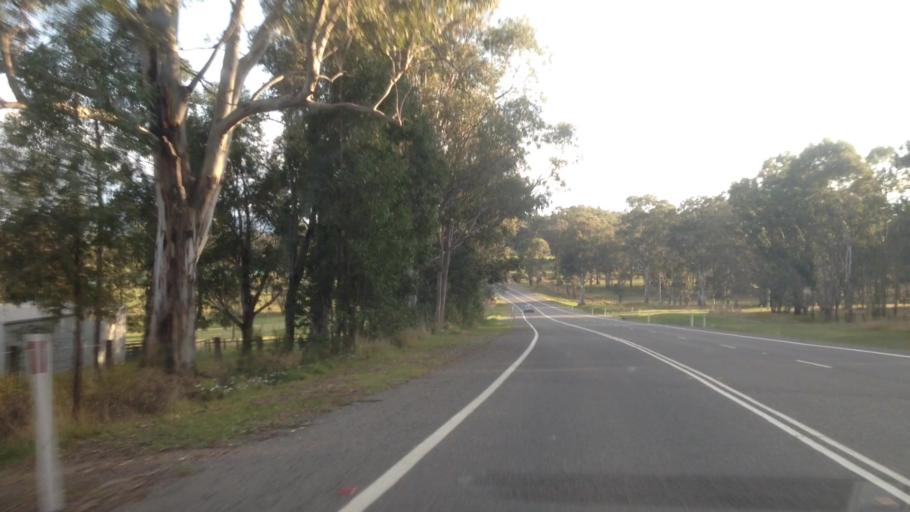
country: AU
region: New South Wales
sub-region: Cessnock
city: Kurri Kurri
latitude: -32.8621
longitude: 151.4823
